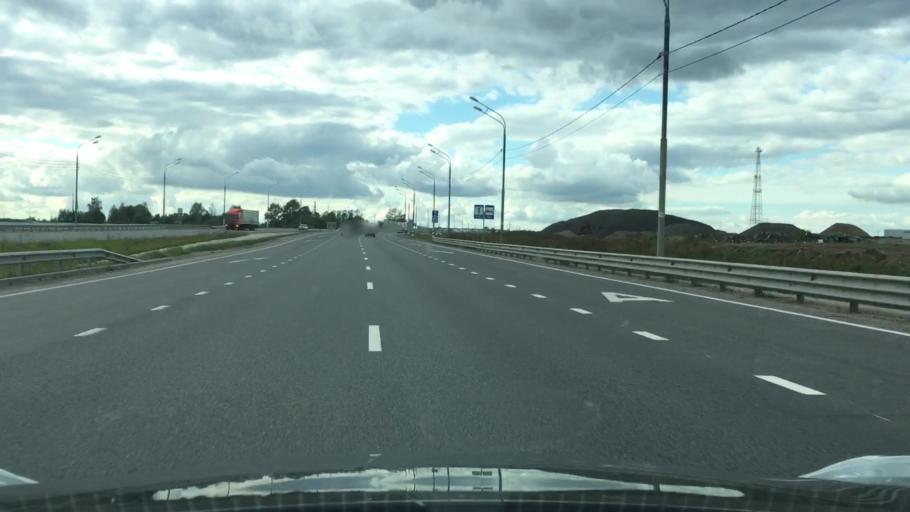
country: RU
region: Tverskaya
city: Tver
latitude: 56.7824
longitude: 35.9543
